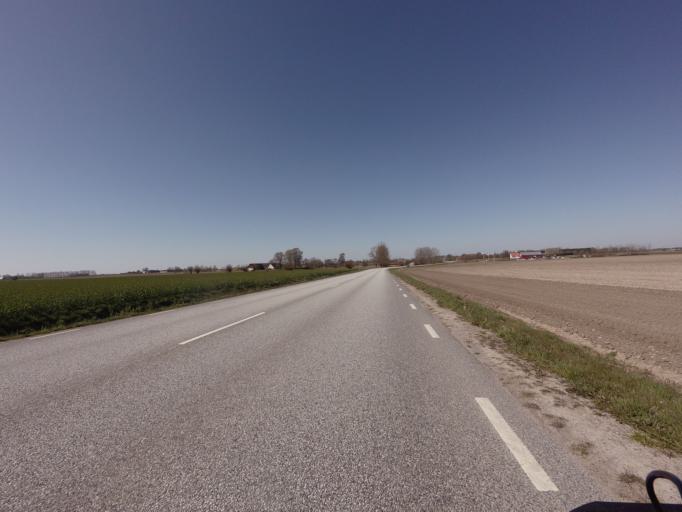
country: SE
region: Skane
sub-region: Malmo
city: Oxie
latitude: 55.4661
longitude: 13.0887
